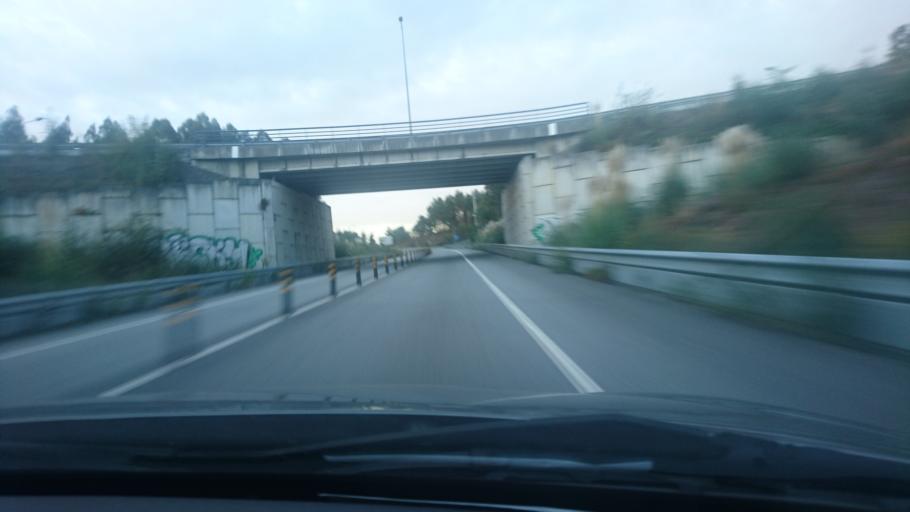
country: PT
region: Aveiro
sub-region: Santa Maria da Feira
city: Arrifana
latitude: 40.9245
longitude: -8.4882
